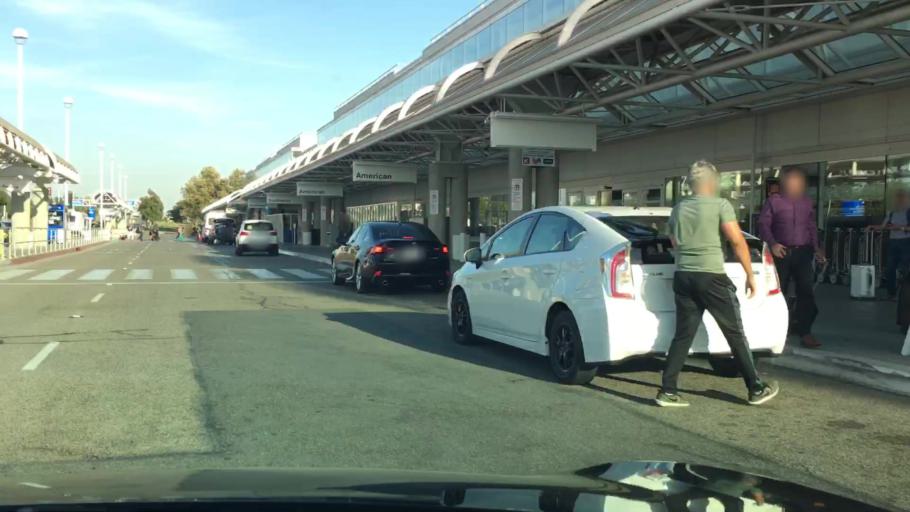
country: US
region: California
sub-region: San Bernardino County
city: Rancho Cucamonga
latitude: 34.0607
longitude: -117.5882
